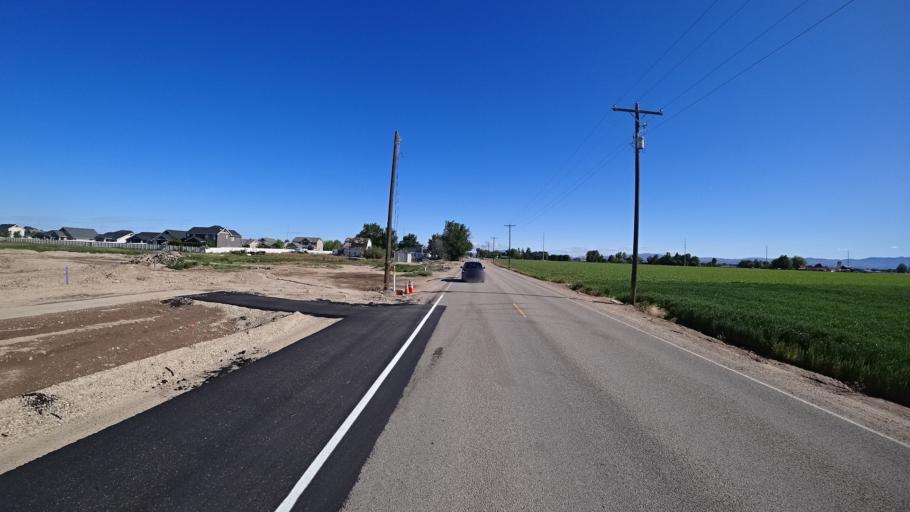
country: US
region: Idaho
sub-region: Ada County
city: Star
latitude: 43.6446
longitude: -116.4537
